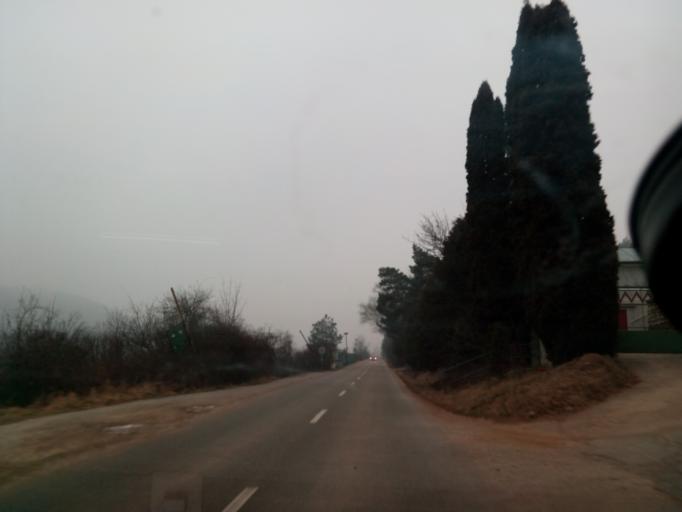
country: SK
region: Kosicky
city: Kosice
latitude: 48.7026
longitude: 21.1592
